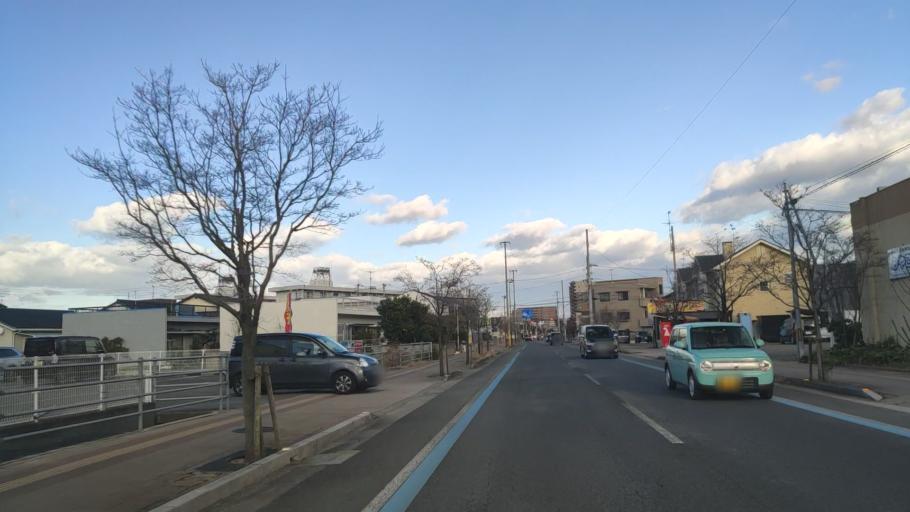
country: JP
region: Ehime
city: Saijo
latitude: 33.9161
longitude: 133.1754
